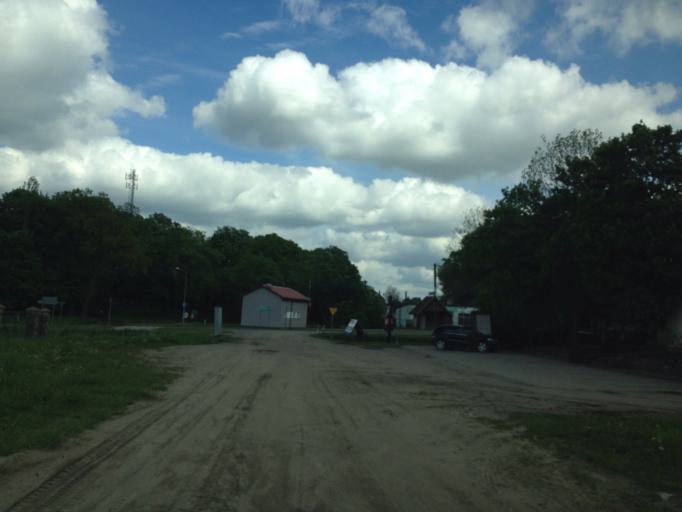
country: PL
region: Warmian-Masurian Voivodeship
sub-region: Powiat nidzicki
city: Nidzica
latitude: 53.4402
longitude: 20.3276
